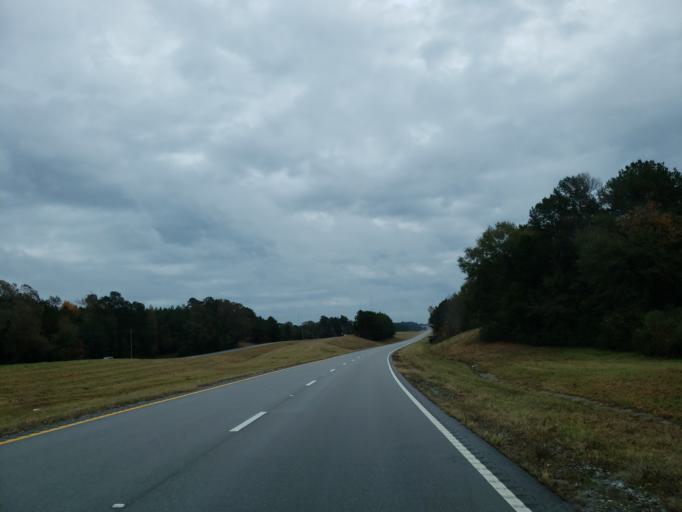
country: US
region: Mississippi
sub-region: Wayne County
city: Waynesboro
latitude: 31.6954
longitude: -88.7213
